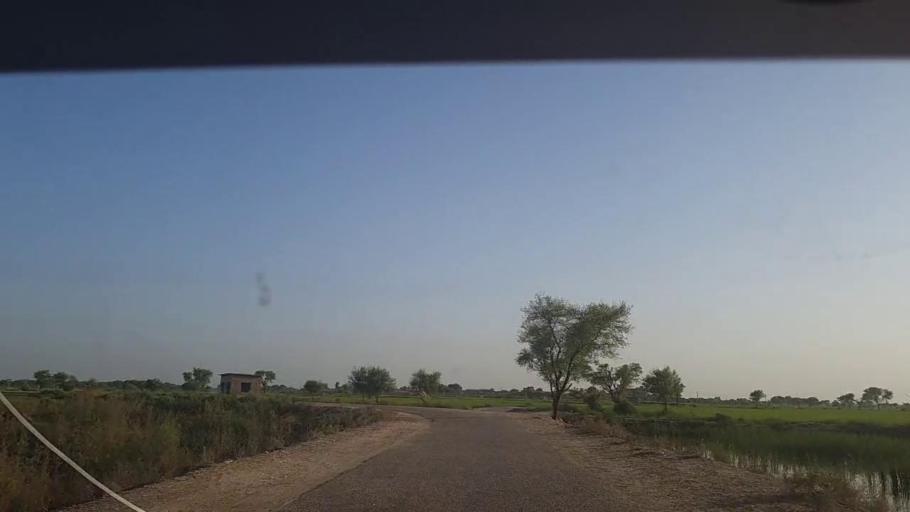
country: PK
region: Sindh
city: Thul
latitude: 28.1906
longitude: 68.8719
